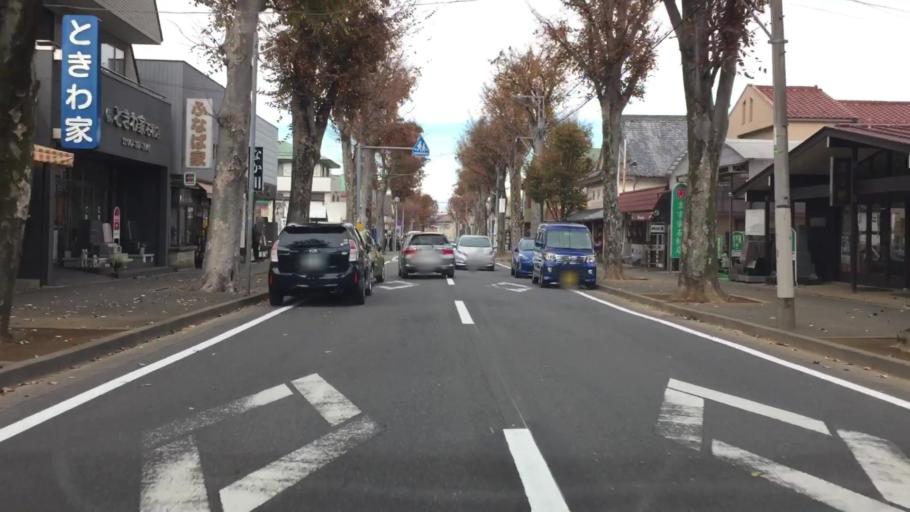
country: JP
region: Chiba
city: Matsudo
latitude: 35.7838
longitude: 139.9463
